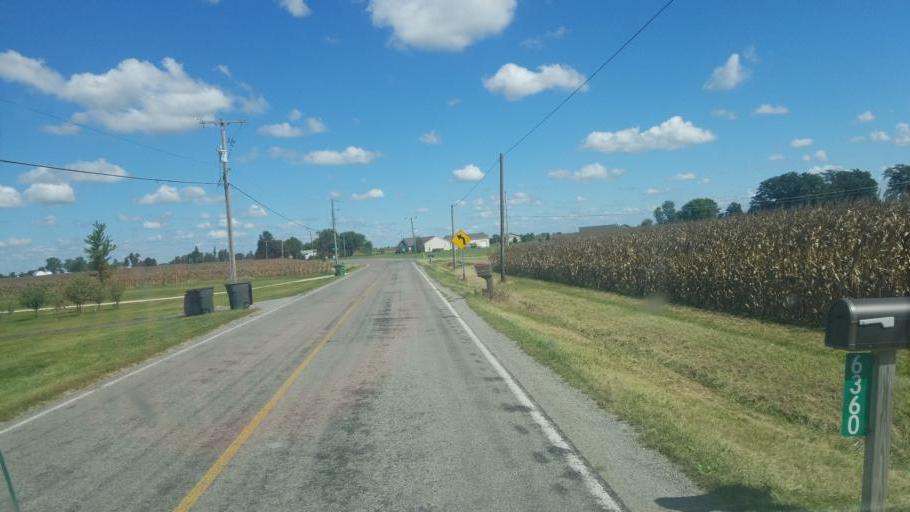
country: US
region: Ohio
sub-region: Madison County
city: Plain City
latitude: 40.0305
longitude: -83.3710
